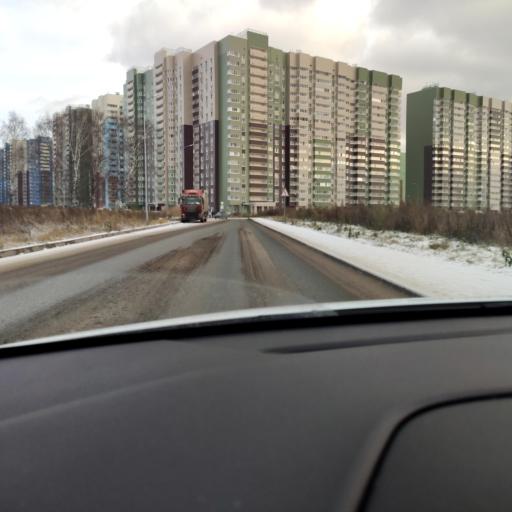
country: RU
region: Tatarstan
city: Osinovo
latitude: 55.8660
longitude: 48.8684
